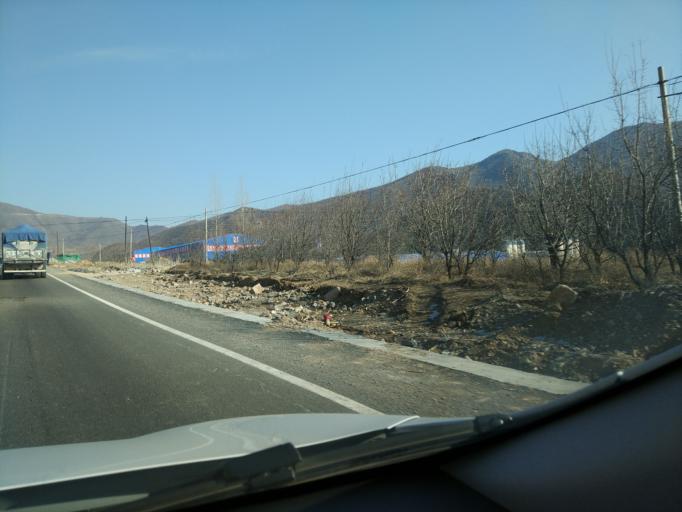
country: CN
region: Hebei
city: Shacheng
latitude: 40.5417
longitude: 115.6417
